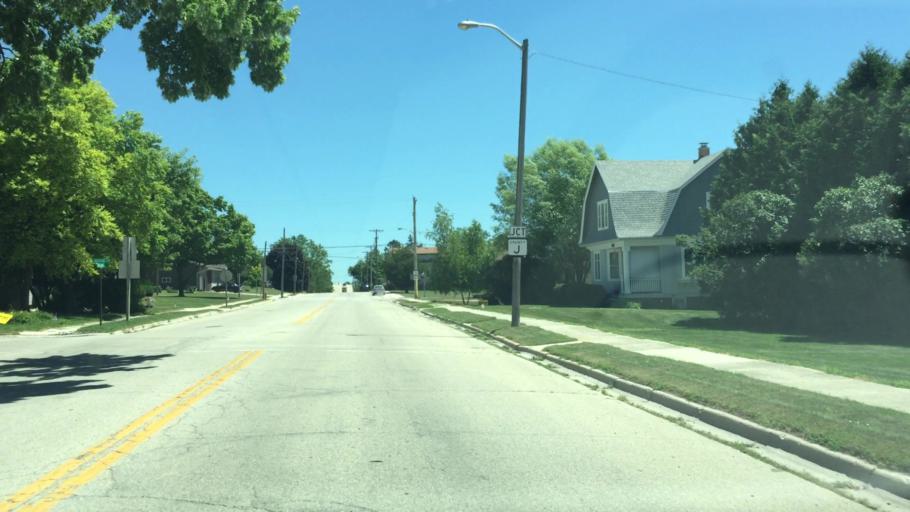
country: US
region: Wisconsin
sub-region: Calumet County
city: New Holstein
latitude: 43.9497
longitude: -88.0839
